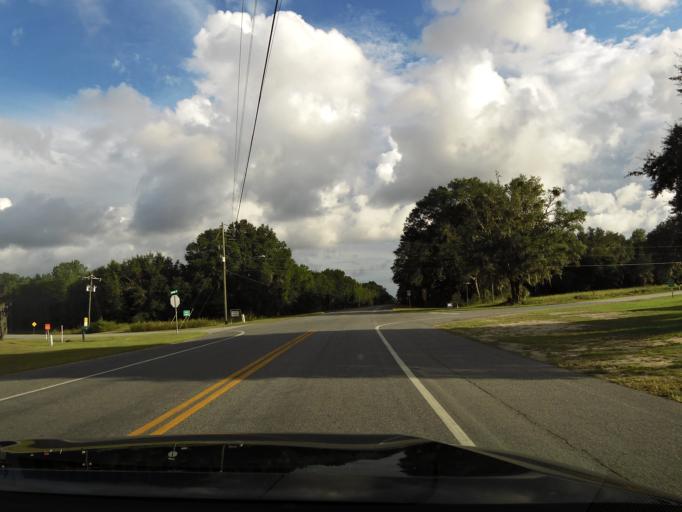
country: US
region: Georgia
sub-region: Liberty County
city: Midway
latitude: 31.7032
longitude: -81.4141
